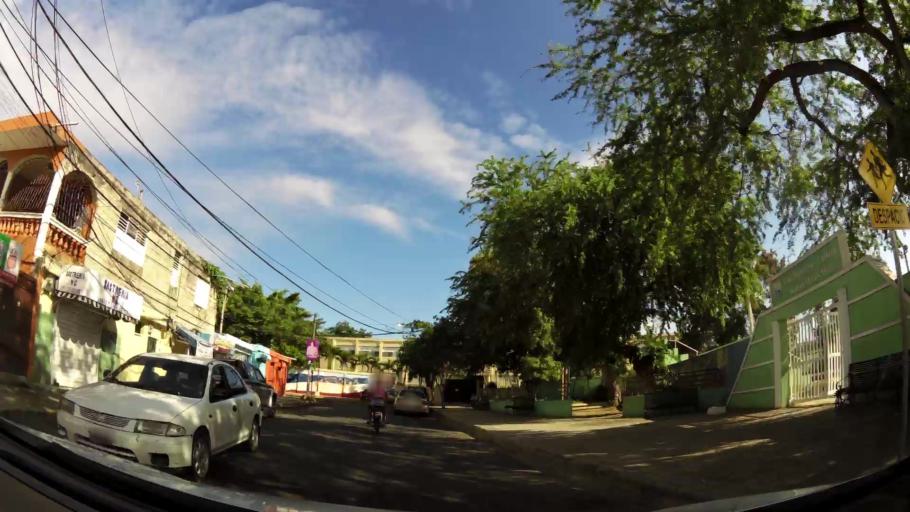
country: DO
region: Santo Domingo
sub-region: Santo Domingo
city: Santo Domingo Este
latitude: 18.4876
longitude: -69.8783
